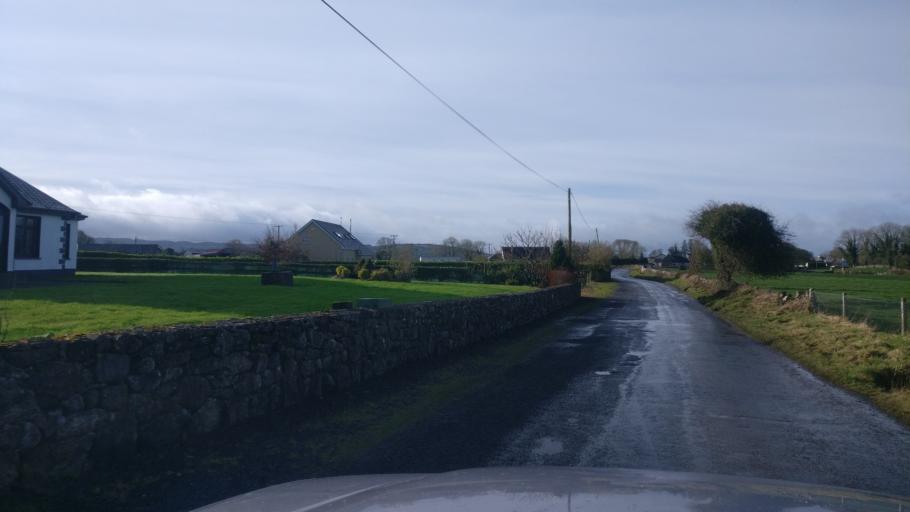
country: IE
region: Connaught
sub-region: County Galway
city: Loughrea
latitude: 53.1980
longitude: -8.6144
